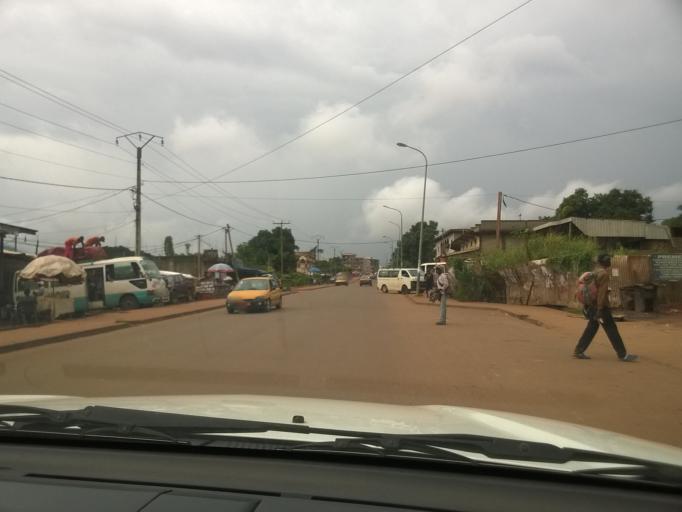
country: CM
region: Centre
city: Yaounde
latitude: 3.9073
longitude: 11.5252
